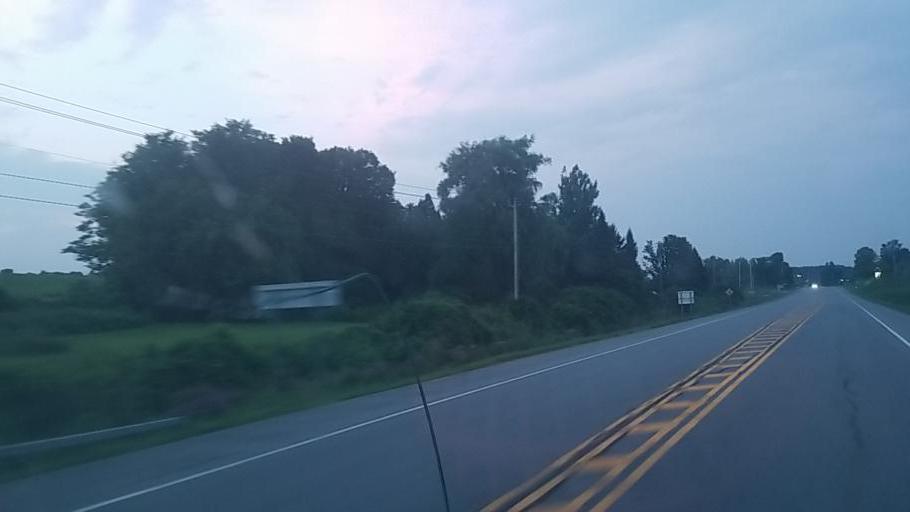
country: US
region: New York
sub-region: Montgomery County
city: Fonda
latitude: 42.9822
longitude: -74.3898
